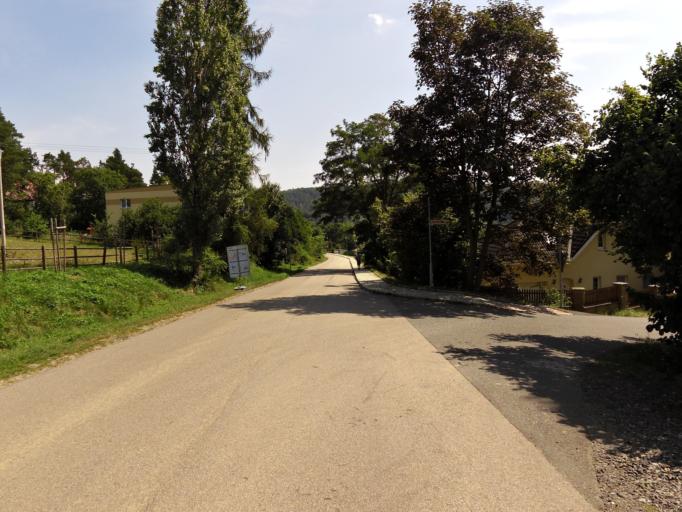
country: CZ
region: Central Bohemia
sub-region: Okres Benesov
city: Cercany
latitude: 49.8703
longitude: 14.7096
